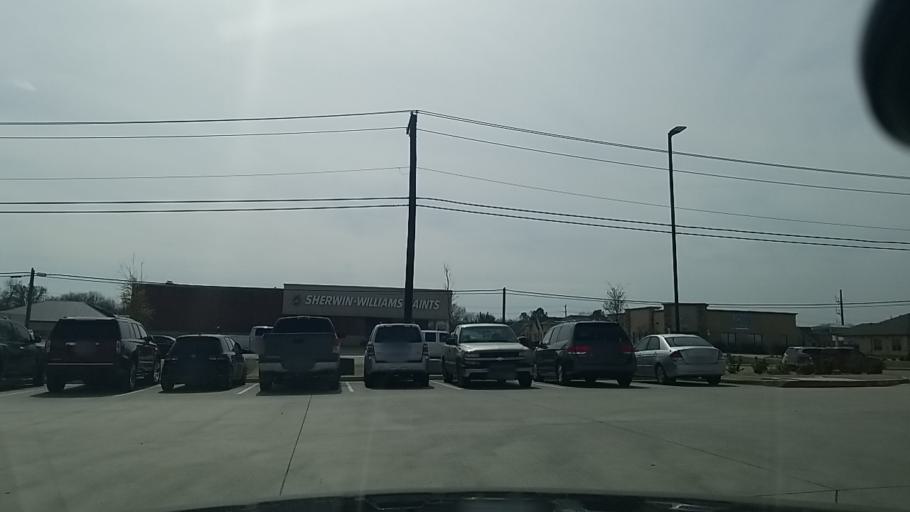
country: US
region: Texas
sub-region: Denton County
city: Denton
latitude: 33.2301
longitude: -97.1580
